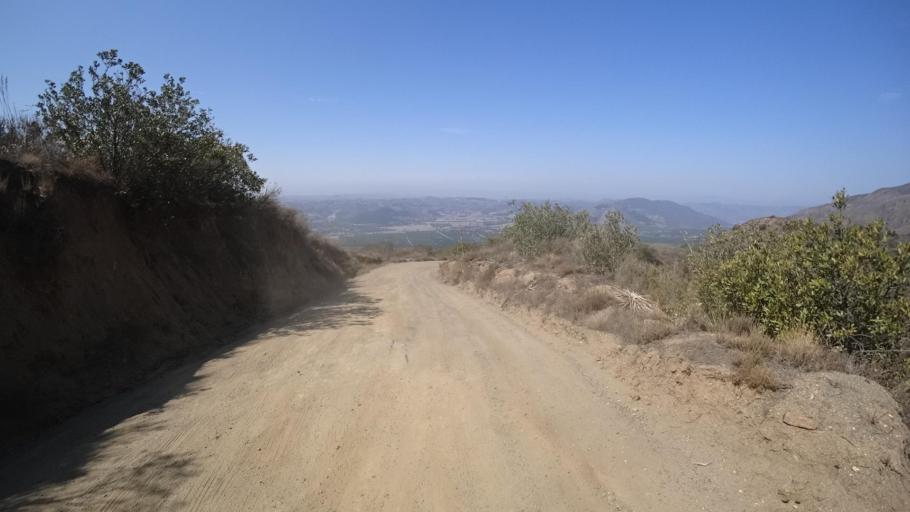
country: US
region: California
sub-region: San Diego County
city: Valley Center
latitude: 33.3314
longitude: -116.9571
